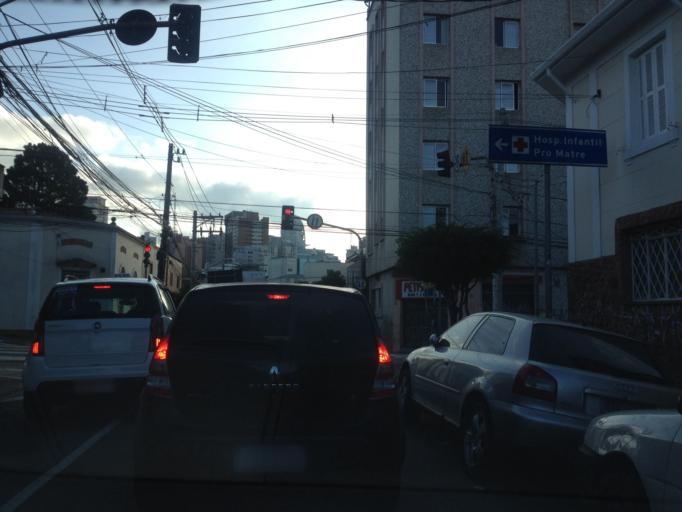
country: BR
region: Sao Paulo
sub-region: Sao Paulo
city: Sao Paulo
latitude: -23.5579
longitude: -46.6470
